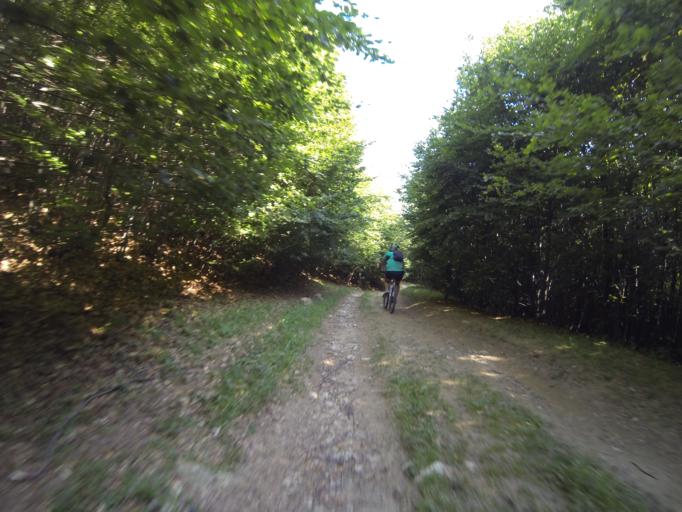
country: RO
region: Valcea
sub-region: Comuna Vaideeni
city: Vaideeni
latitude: 45.2289
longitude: 23.9645
